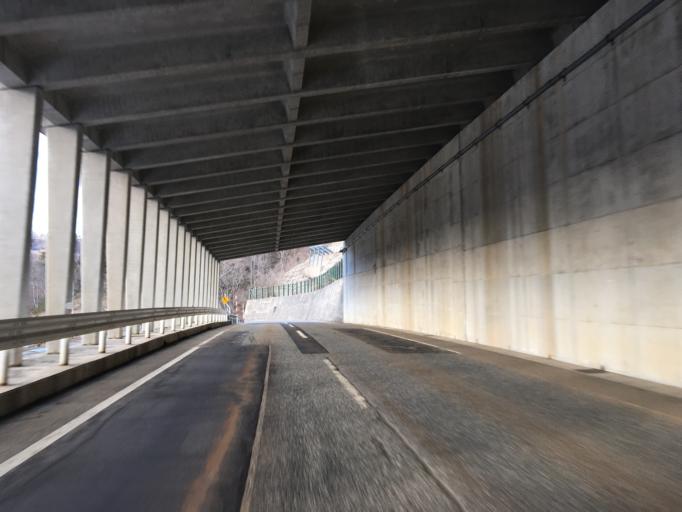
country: JP
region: Yamagata
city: Yonezawa
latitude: 37.9364
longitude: 139.9138
